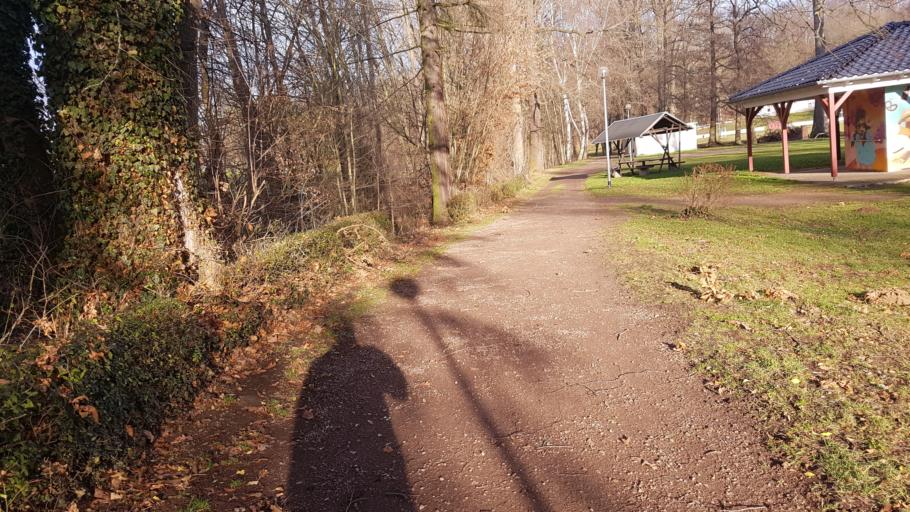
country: DE
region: Saxony
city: Ostrau
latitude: 51.1681
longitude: 13.1636
